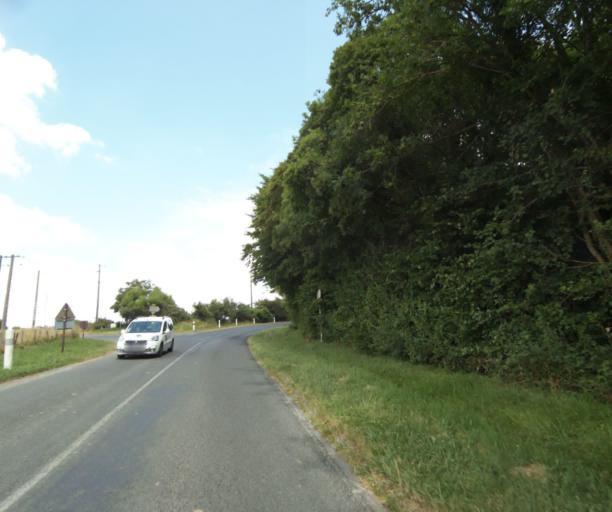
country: FR
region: Ile-de-France
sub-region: Departement de Seine-et-Marne
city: Hericy
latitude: 48.4474
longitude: 2.7933
